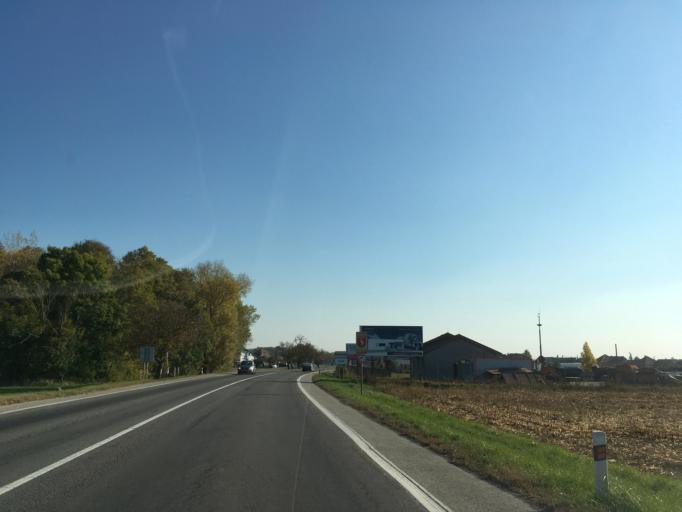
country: SK
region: Trnavsky
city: Dunajska Streda
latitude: 47.9691
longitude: 17.6764
